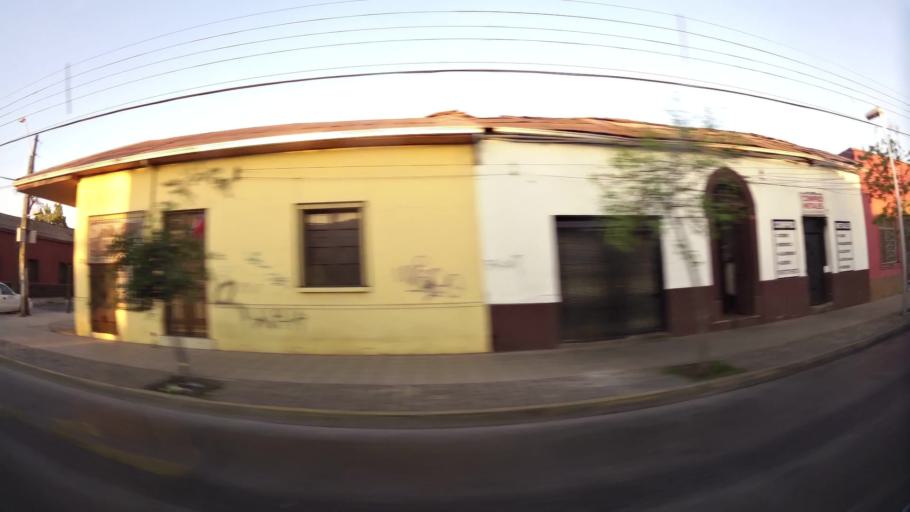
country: CL
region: Santiago Metropolitan
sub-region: Provincia de Santiago
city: Santiago
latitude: -33.4638
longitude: -70.6722
